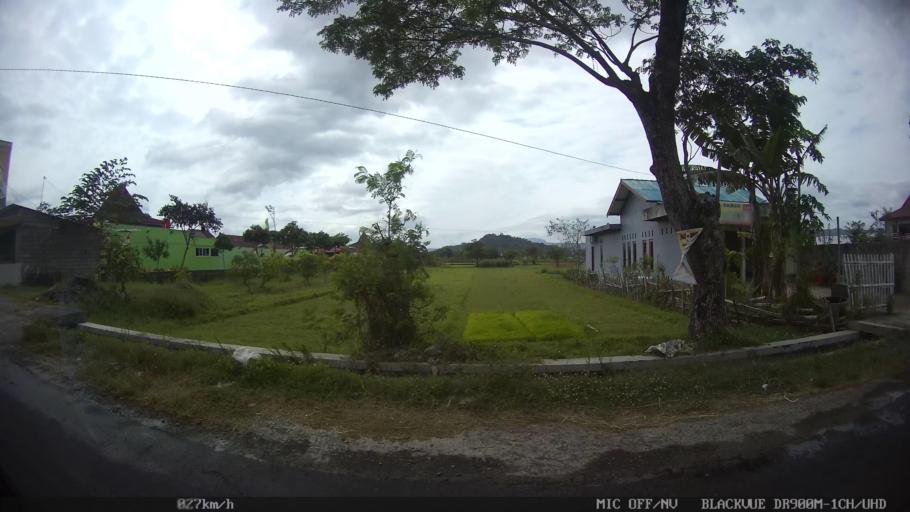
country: ID
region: Daerah Istimewa Yogyakarta
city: Depok
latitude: -7.8211
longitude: 110.4426
